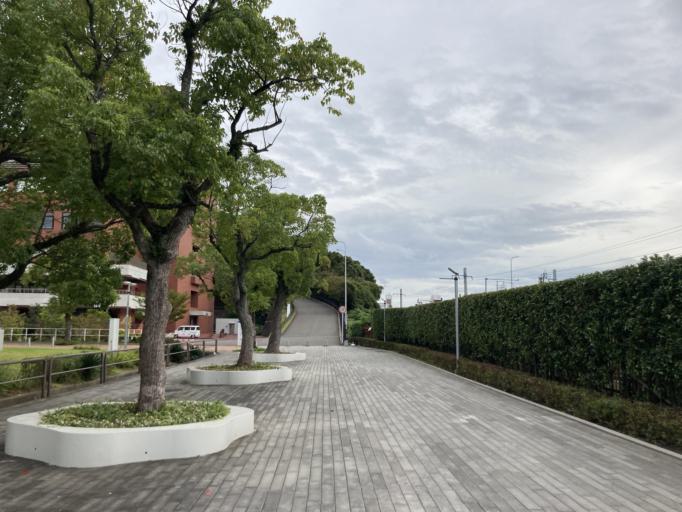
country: JP
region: Fukuoka
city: Shingu
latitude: 33.6719
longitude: 130.4427
